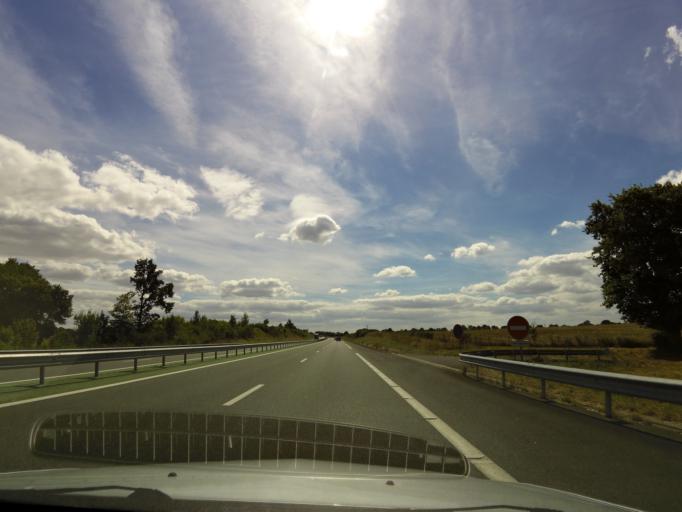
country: FR
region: Pays de la Loire
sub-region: Departement de la Vendee
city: Les Essarts
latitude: 46.7777
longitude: -1.2601
